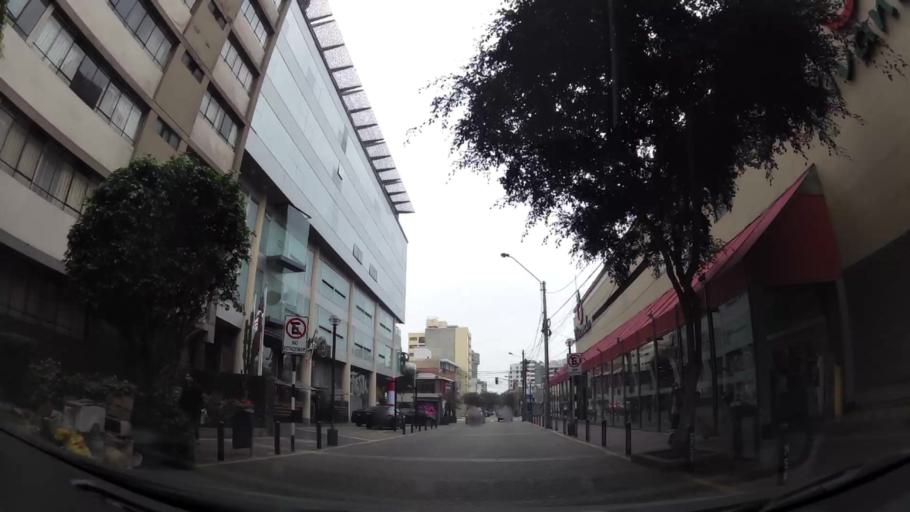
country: PE
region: Lima
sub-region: Lima
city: San Isidro
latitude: -12.1241
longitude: -77.0280
